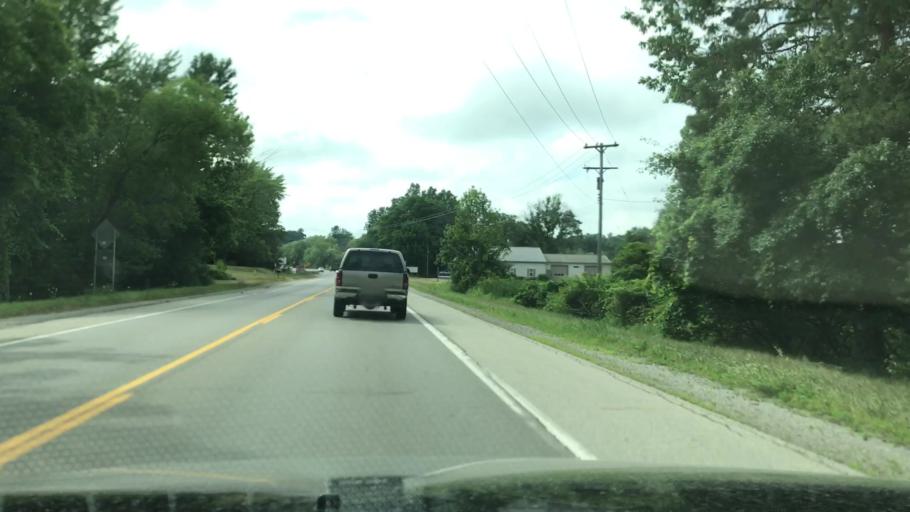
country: US
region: Michigan
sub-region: Ottawa County
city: Spring Lake
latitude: 43.0751
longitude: -86.1661
